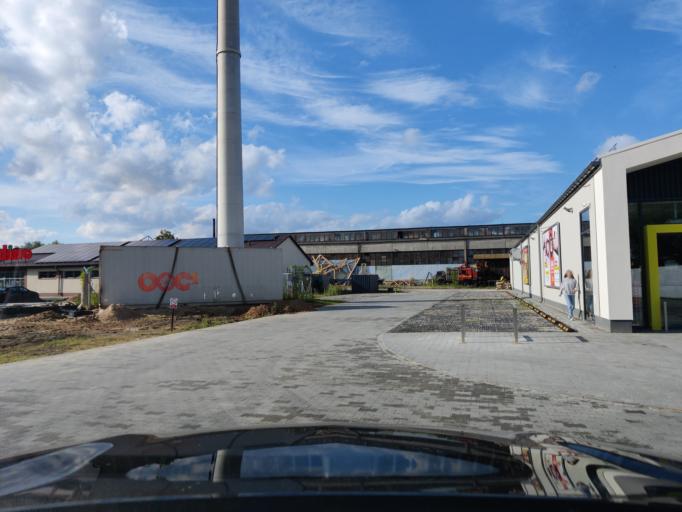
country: PL
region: Masovian Voivodeship
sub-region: Powiat pultuski
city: Pultusk
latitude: 52.6890
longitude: 21.1062
